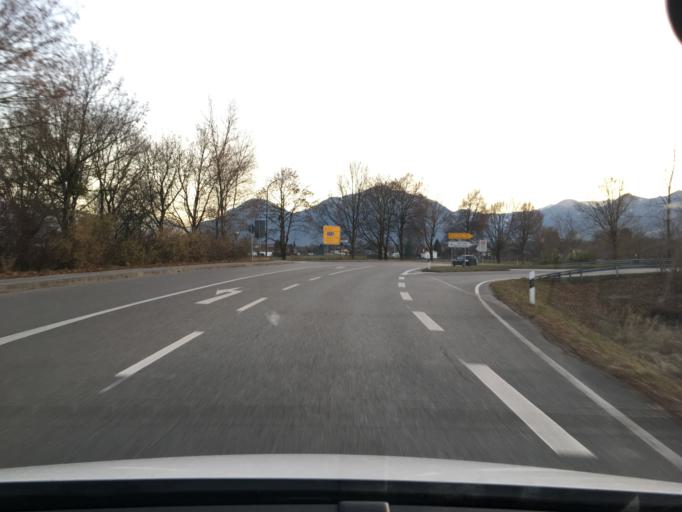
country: DE
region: Bavaria
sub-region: Upper Bavaria
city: Raubling
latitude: 47.7744
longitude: 12.1064
